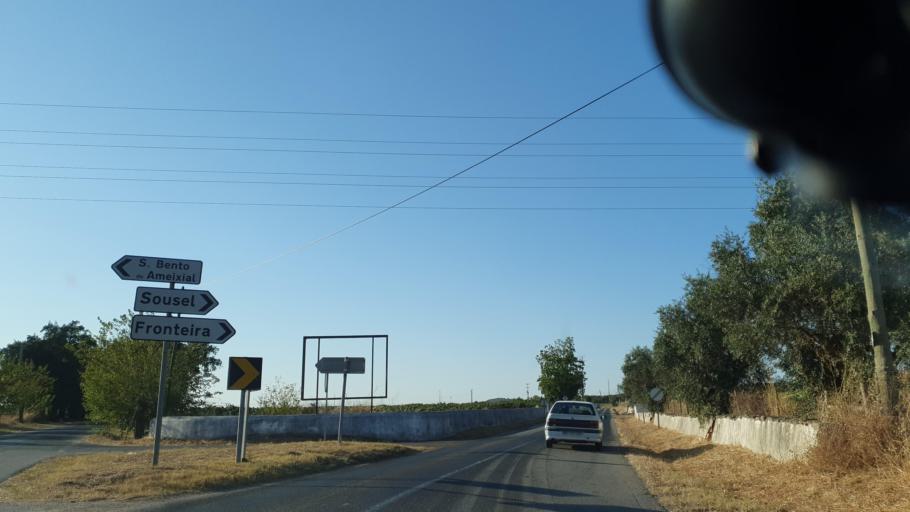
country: PT
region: Evora
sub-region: Estremoz
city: Estremoz
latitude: 38.8501
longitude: -7.6110
